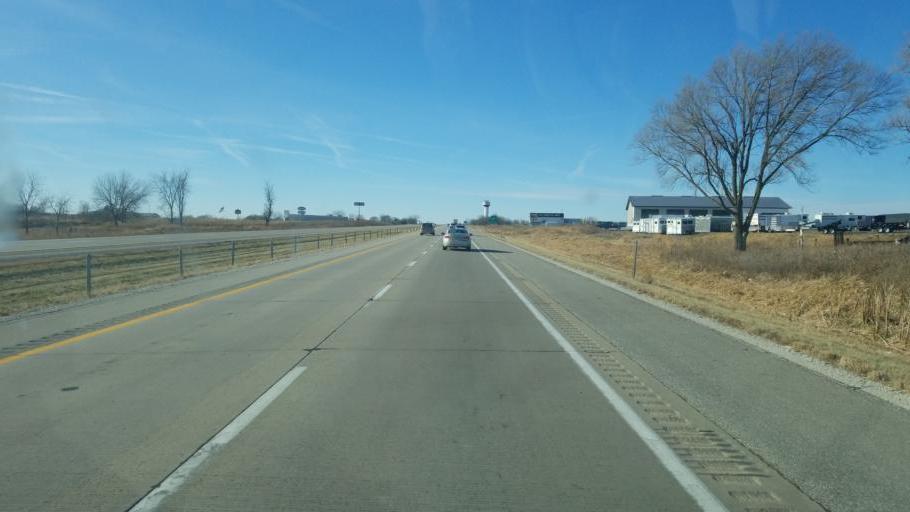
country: US
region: Iowa
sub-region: Dallas County
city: De Soto
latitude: 41.5415
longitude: -94.0015
